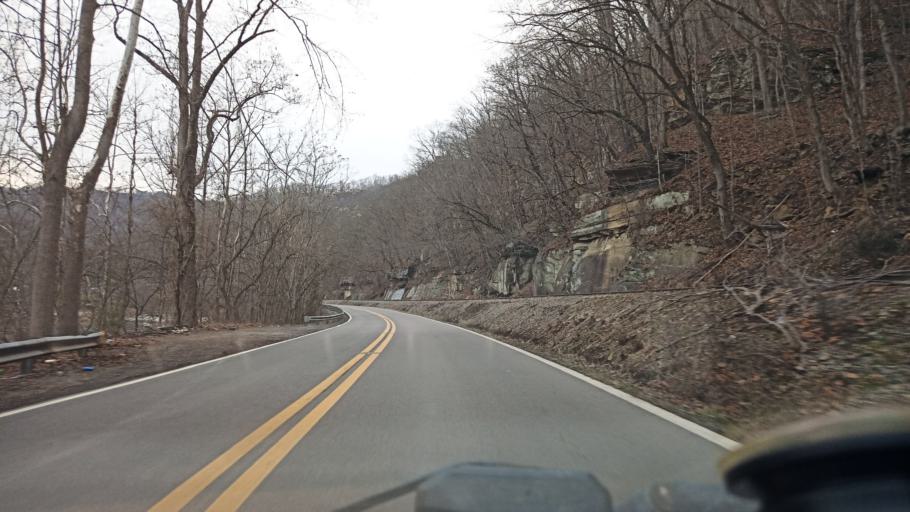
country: US
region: West Virginia
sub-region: Logan County
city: Mallory
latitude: 37.6934
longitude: -81.8605
